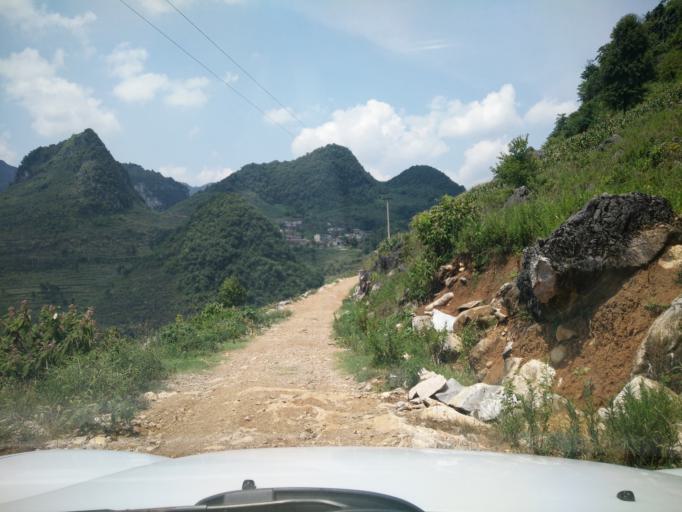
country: CN
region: Guangxi Zhuangzu Zizhiqu
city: Xinzhou
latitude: 25.0045
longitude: 105.7026
